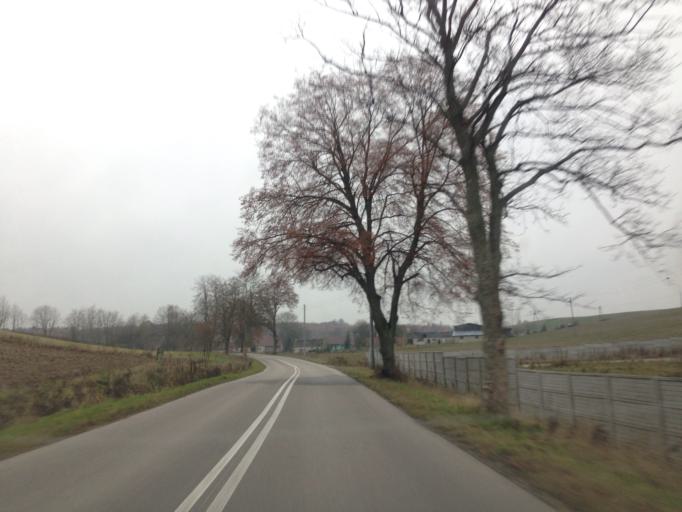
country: PL
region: Pomeranian Voivodeship
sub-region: Powiat gdanski
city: Przywidz
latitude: 54.1891
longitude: 18.3423
